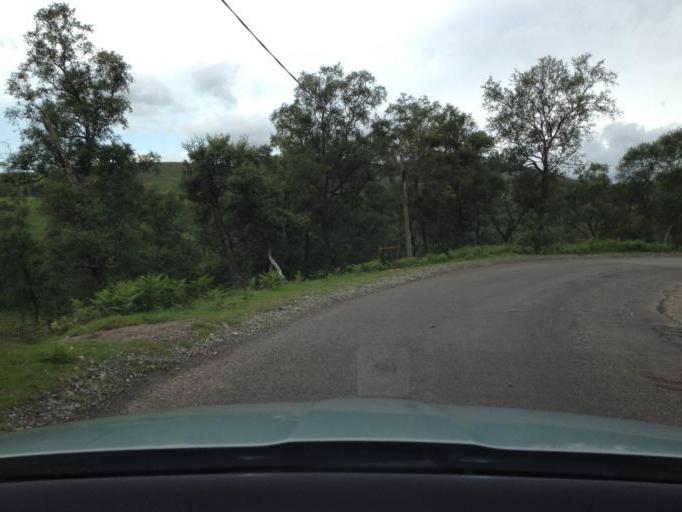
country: GB
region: Scotland
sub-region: Aberdeenshire
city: Aboyne
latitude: 56.8945
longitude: -2.7916
